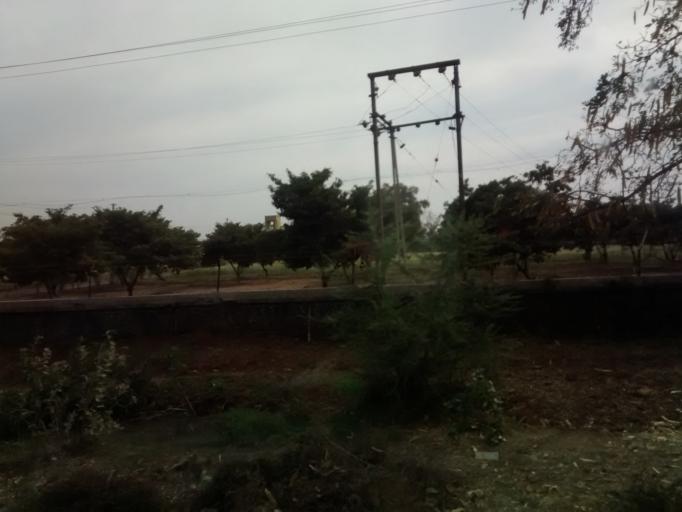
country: IN
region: Gujarat
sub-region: Gandhinagar
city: Ghandinagar
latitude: 23.2838
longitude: 72.6419
